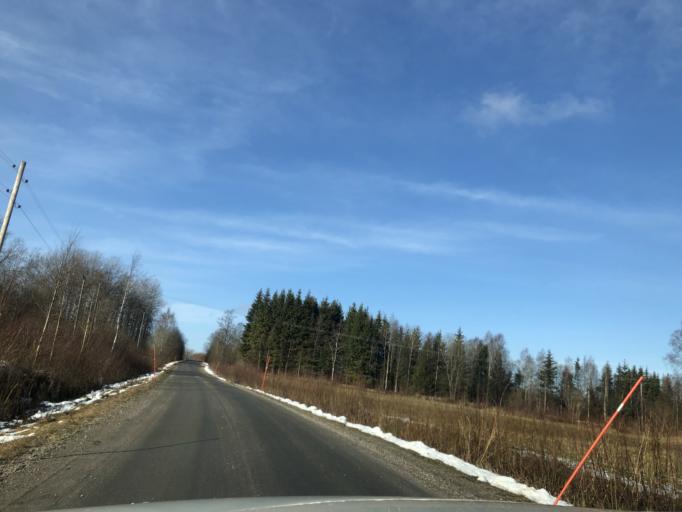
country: SE
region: Vaestra Goetaland
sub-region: Ulricehamns Kommun
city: Ulricehamn
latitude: 57.7954
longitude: 13.4548
